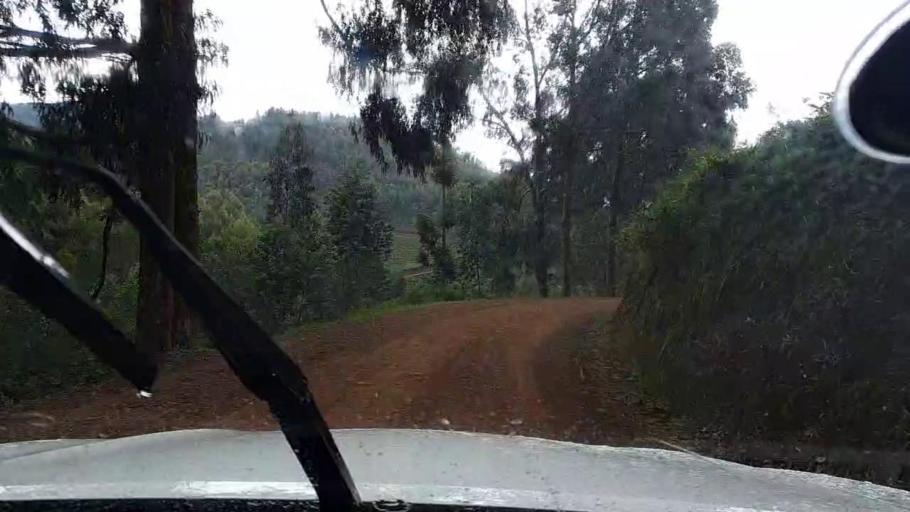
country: RW
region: Western Province
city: Kibuye
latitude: -2.1568
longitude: 29.4318
